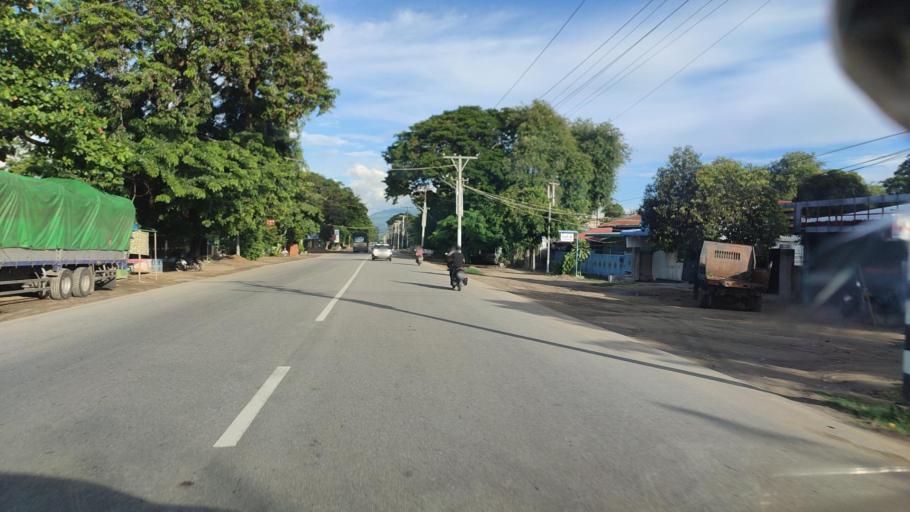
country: MM
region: Mandalay
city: Yamethin
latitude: 20.1243
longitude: 96.2089
